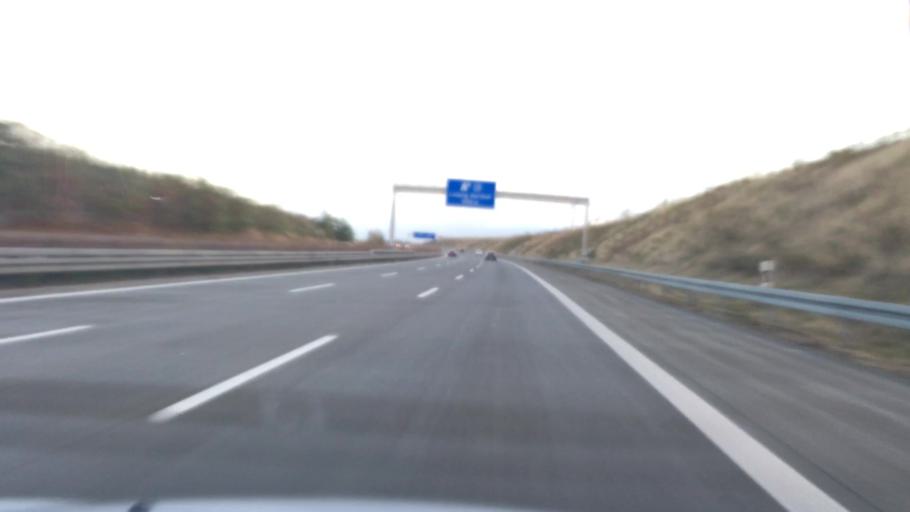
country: DE
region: Saxony
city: Taucha
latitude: 51.3772
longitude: 12.4559
